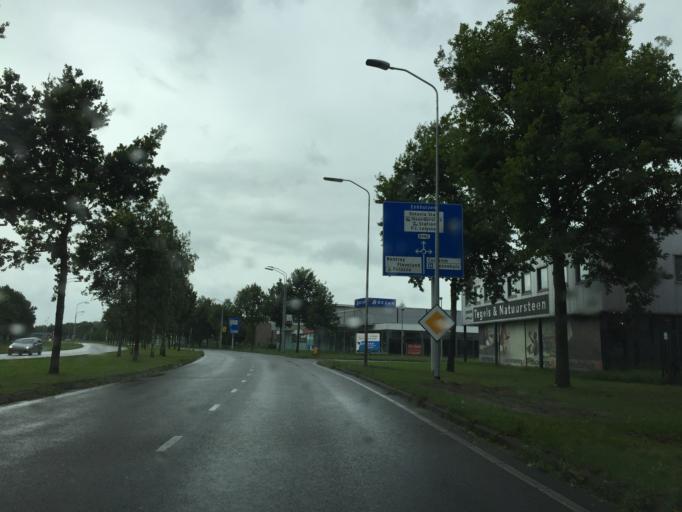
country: NL
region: Flevoland
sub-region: Gemeente Lelystad
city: Lelystad
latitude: 52.4920
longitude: 5.4855
